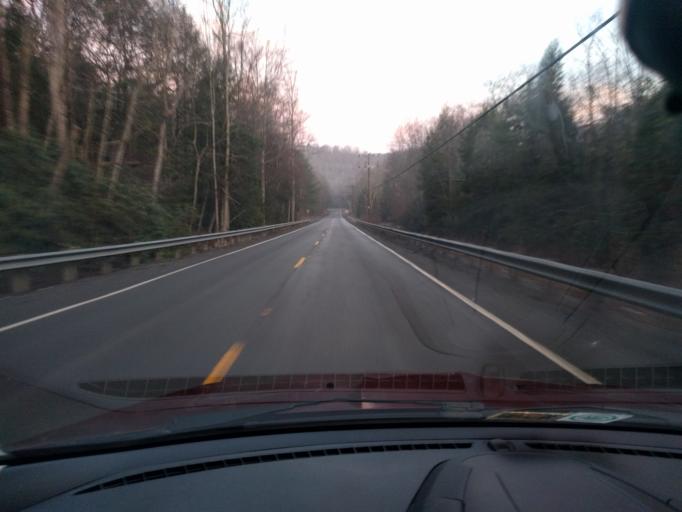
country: US
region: West Virginia
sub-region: Greenbrier County
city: Rainelle
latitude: 38.0471
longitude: -80.9259
